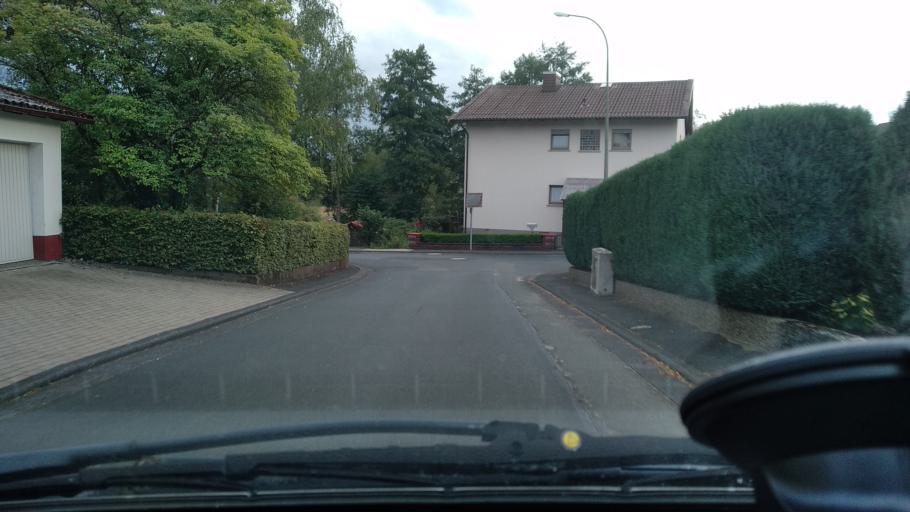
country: DE
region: Hesse
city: Dillenburg
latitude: 50.7730
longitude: 8.2928
